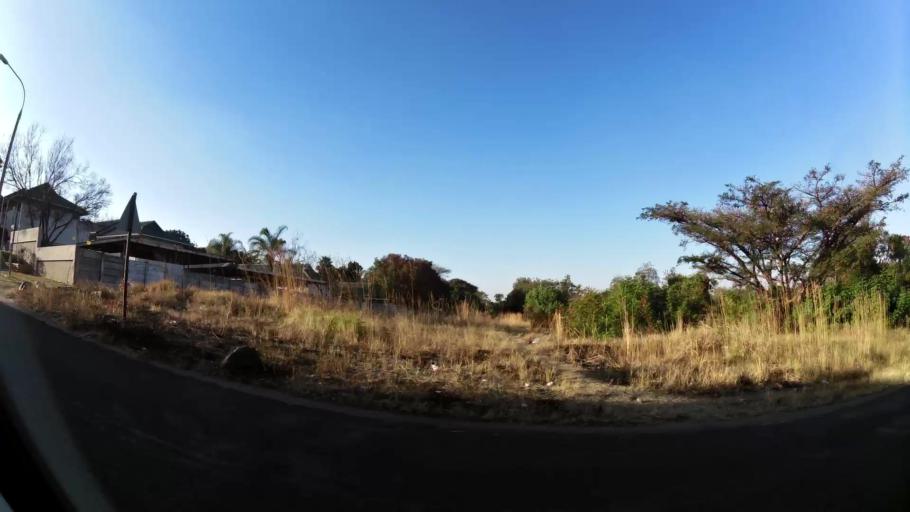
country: ZA
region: North-West
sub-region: Bojanala Platinum District Municipality
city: Rustenburg
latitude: -25.6849
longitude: 27.2056
